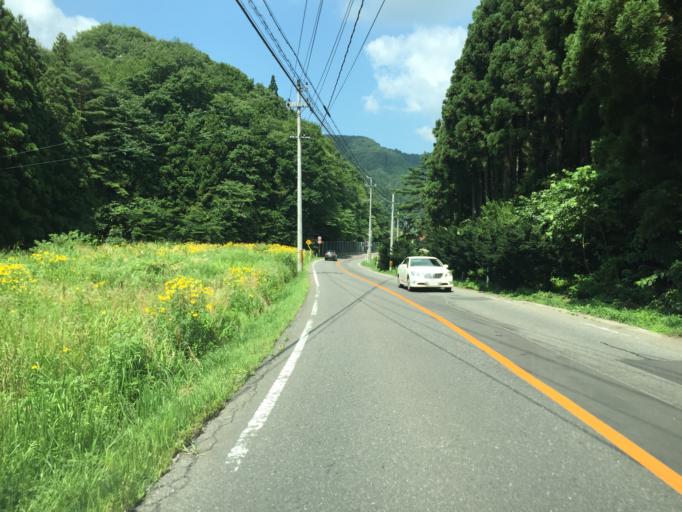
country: JP
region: Fukushima
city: Inawashiro
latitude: 37.3961
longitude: 140.0751
